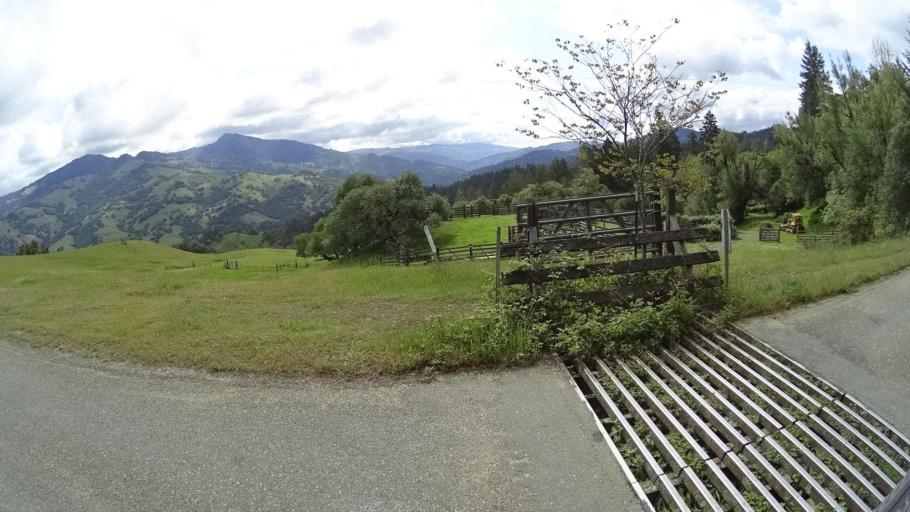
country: US
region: California
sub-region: Humboldt County
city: Redway
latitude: 40.1519
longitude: -123.6244
